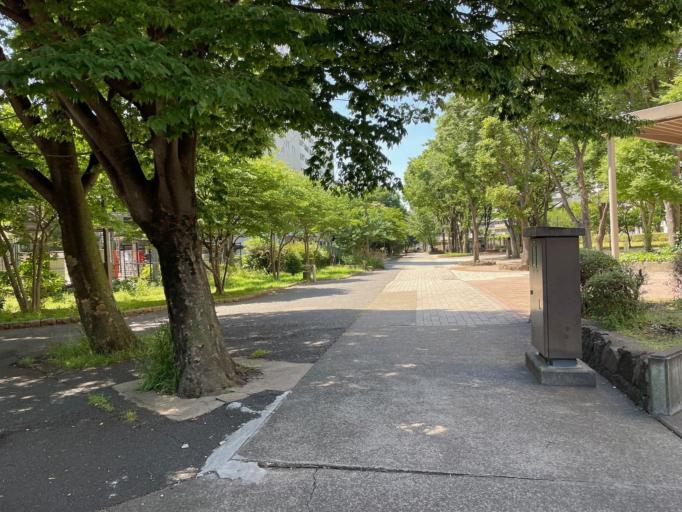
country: JP
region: Tokyo
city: Mitaka-shi
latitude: 35.6569
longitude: 139.6221
